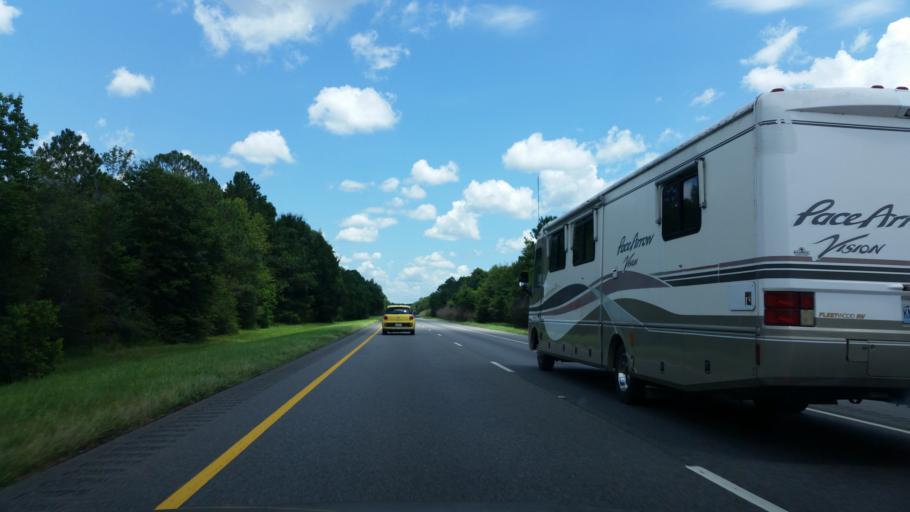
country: US
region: Alabama
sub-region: Baldwin County
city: Loxley
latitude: 30.6351
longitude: -87.6567
